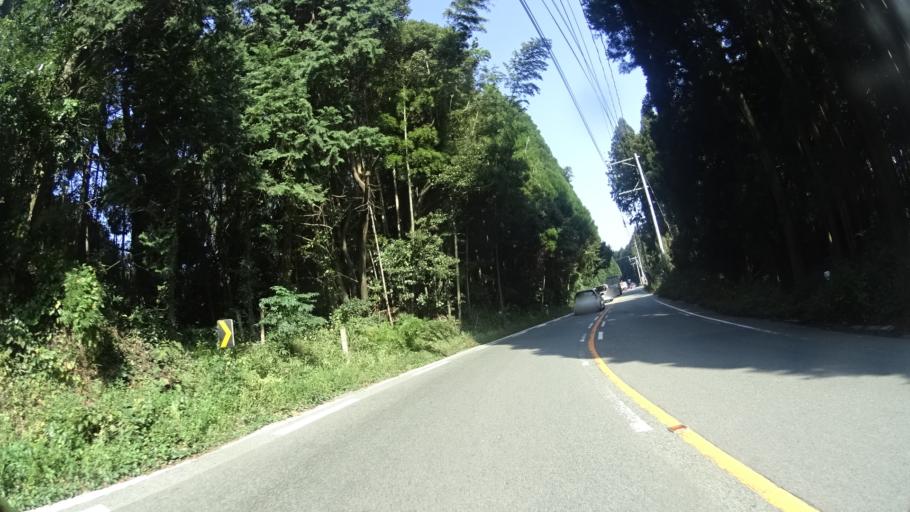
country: JP
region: Kumamoto
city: Ozu
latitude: 32.9085
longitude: 130.9488
